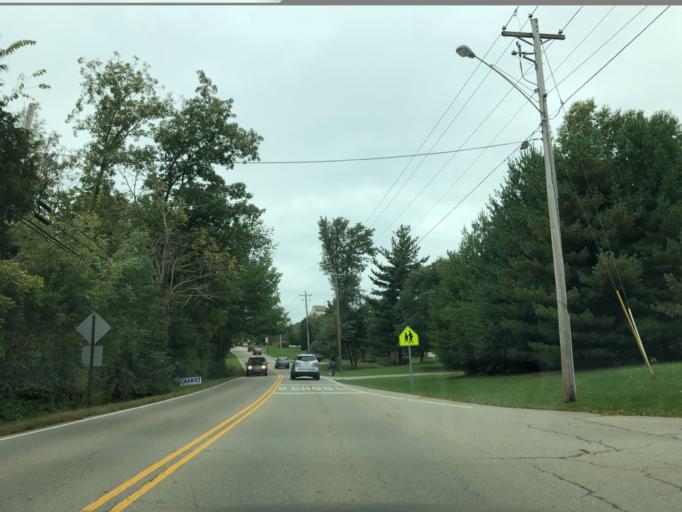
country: US
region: Ohio
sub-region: Warren County
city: Landen
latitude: 39.2993
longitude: -84.2792
